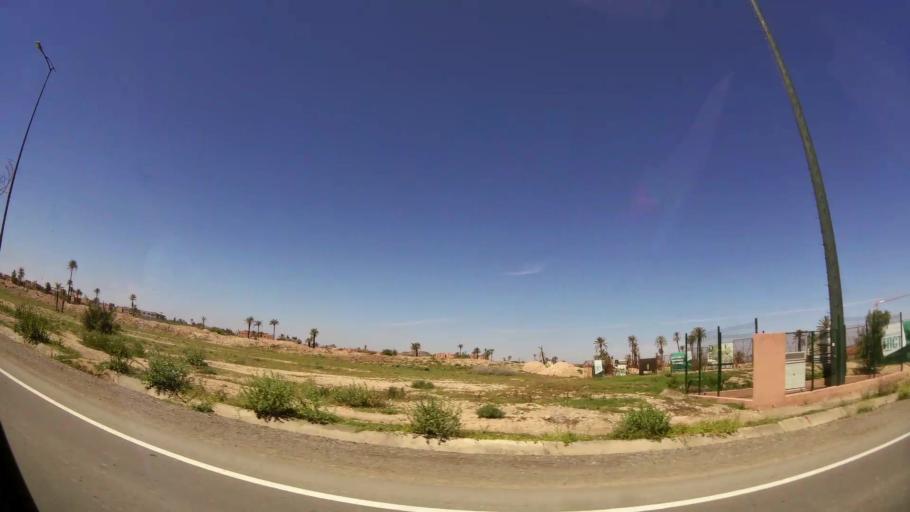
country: MA
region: Marrakech-Tensift-Al Haouz
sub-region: Marrakech
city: Marrakesh
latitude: 31.6717
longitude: -7.9906
